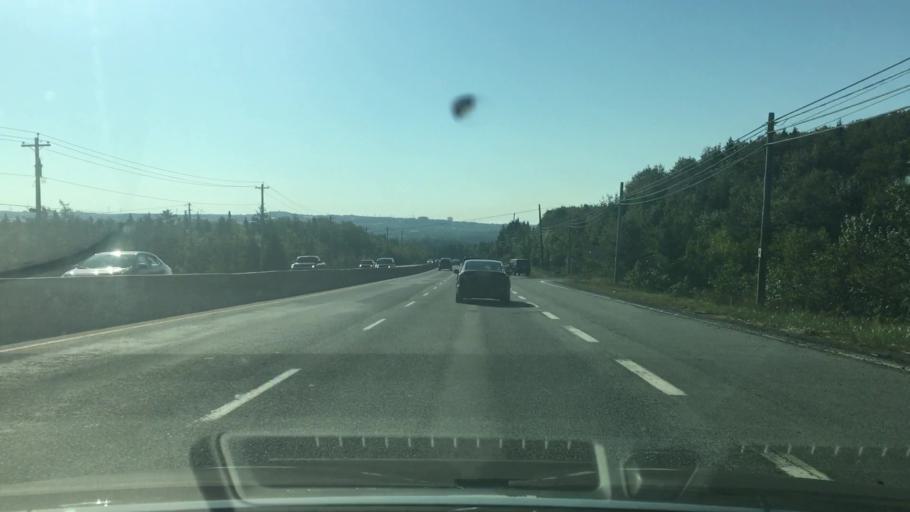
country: CA
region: Nova Scotia
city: Dartmouth
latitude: 44.7130
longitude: -63.6294
